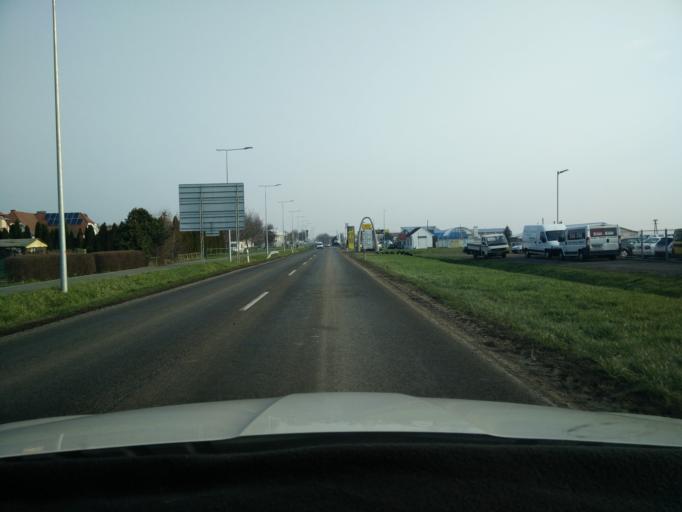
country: HU
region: Tolna
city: Szekszard
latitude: 46.3123
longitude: 18.6949
